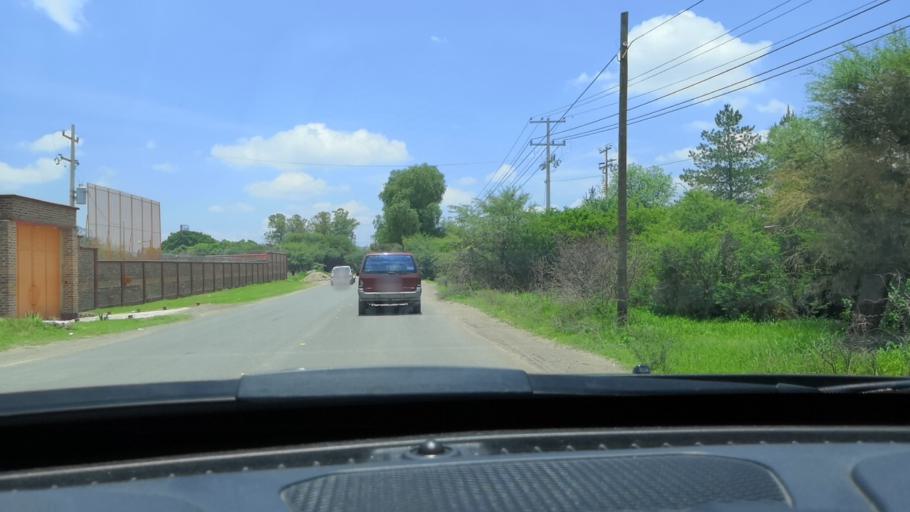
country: MX
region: Guanajuato
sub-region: Leon
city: Ladrilleras del Refugio
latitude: 21.0503
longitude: -101.5640
